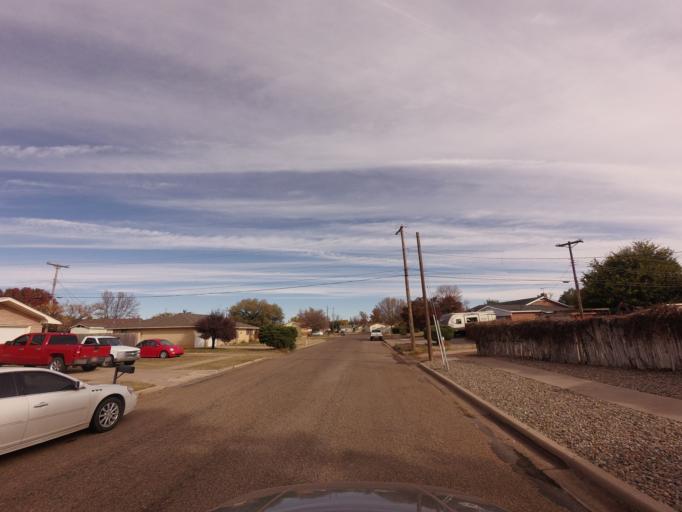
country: US
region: New Mexico
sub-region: Curry County
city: Clovis
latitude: 34.4233
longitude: -103.2175
